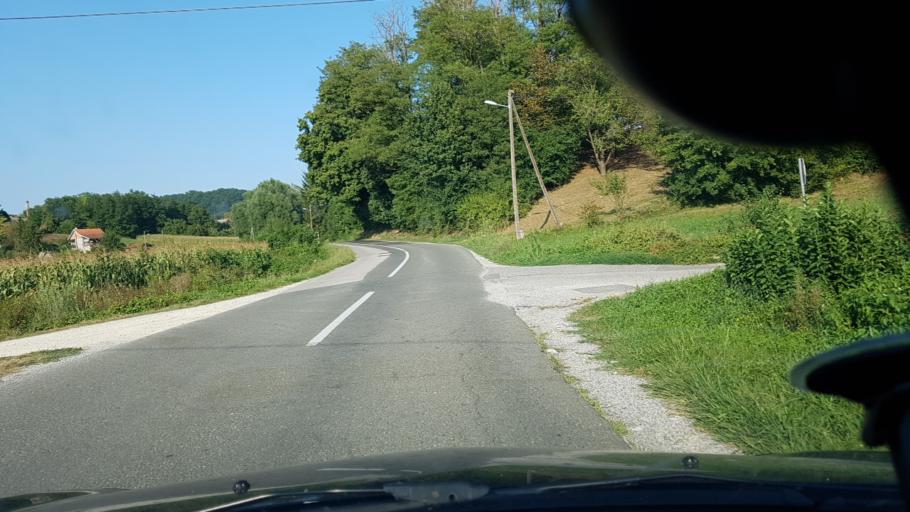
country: SI
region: Bistrica ob Sotli
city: Bistrica ob Sotli
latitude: 46.0215
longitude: 15.7275
